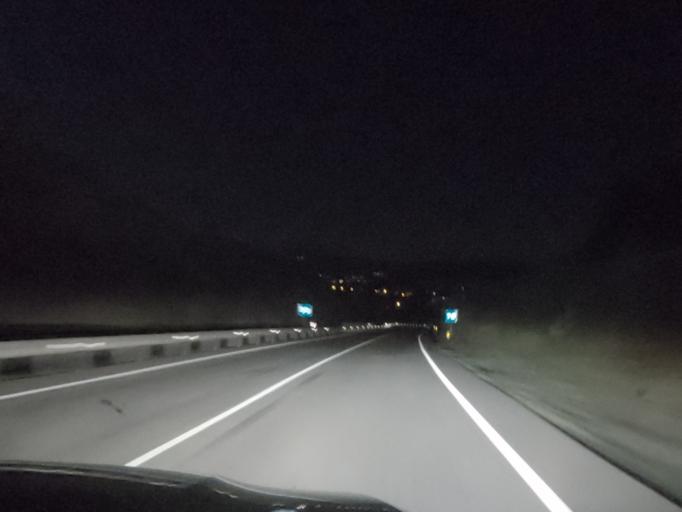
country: ES
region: Galicia
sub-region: Provincia de Ourense
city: Verin
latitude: 41.9597
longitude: -7.5039
